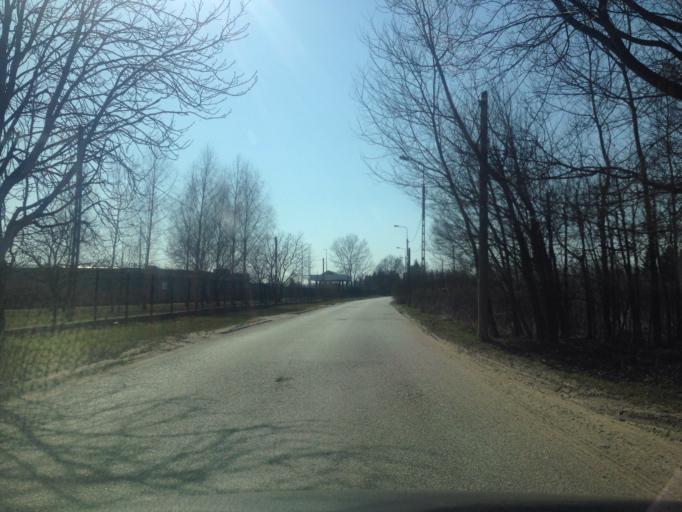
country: PL
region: Masovian Voivodeship
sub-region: Warszawa
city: Wilanow
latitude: 52.1872
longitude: 21.1009
